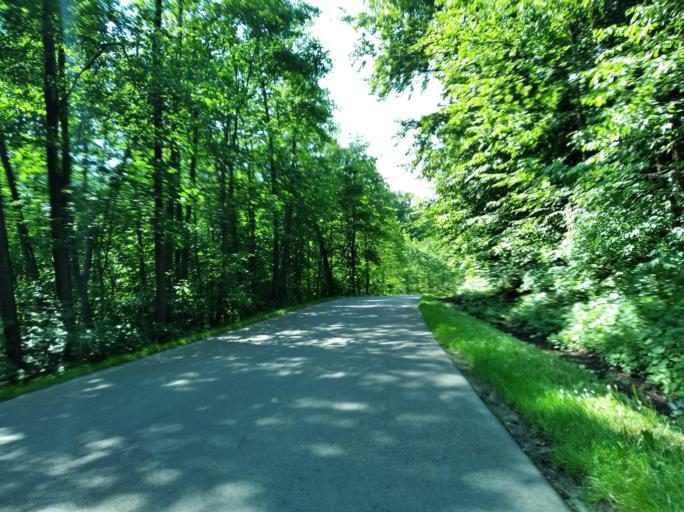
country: PL
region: Subcarpathian Voivodeship
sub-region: Powiat ropczycko-sedziszowski
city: Zagorzyce
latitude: 49.9829
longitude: 21.6469
